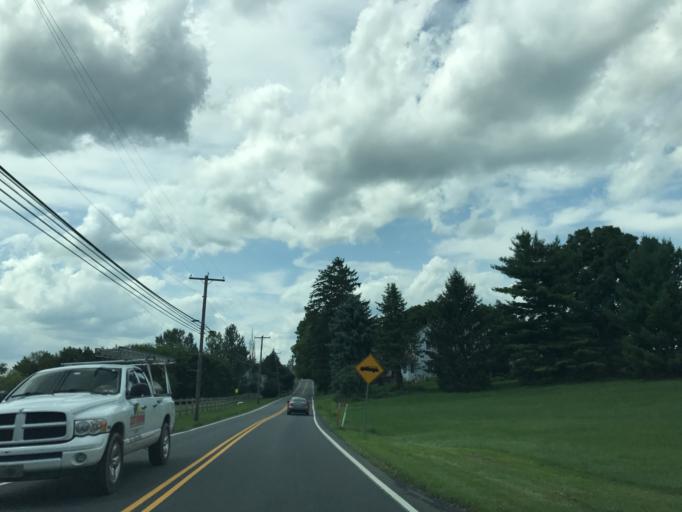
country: US
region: Pennsylvania
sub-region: Lancaster County
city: Penryn
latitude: 40.2042
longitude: -76.3647
